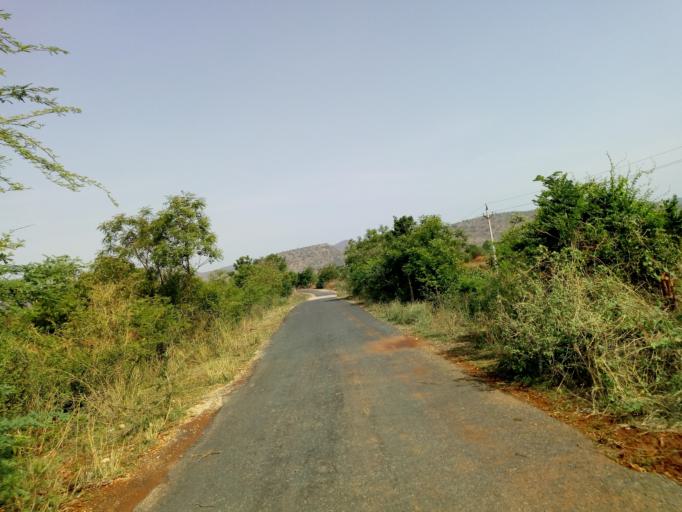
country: IN
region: Andhra Pradesh
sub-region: Prakasam
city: Cumbum
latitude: 15.7139
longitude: 79.0824
